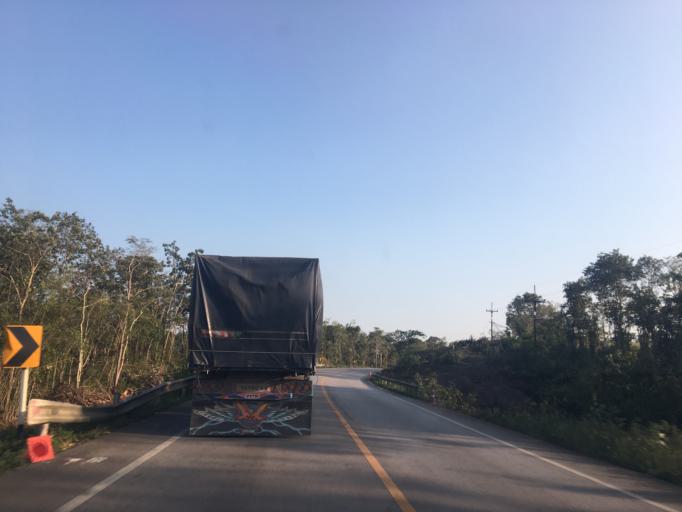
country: TH
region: Lampang
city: Ngao
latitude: 18.6640
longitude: 100.0162
